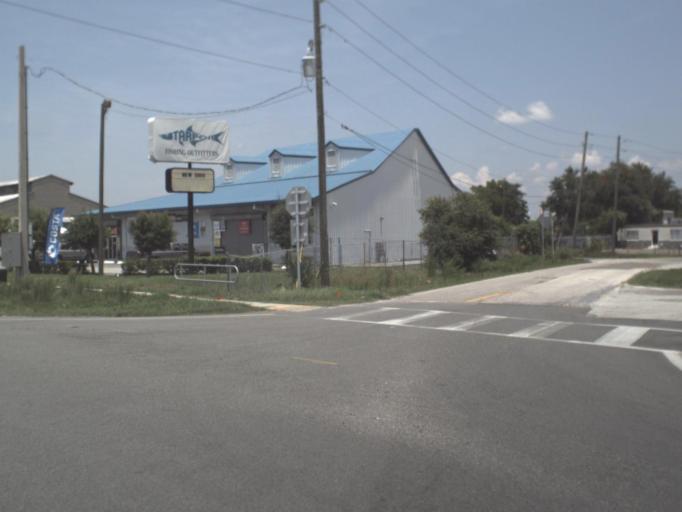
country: US
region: Florida
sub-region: Pasco County
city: Holiday
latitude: 28.1800
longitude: -82.7403
